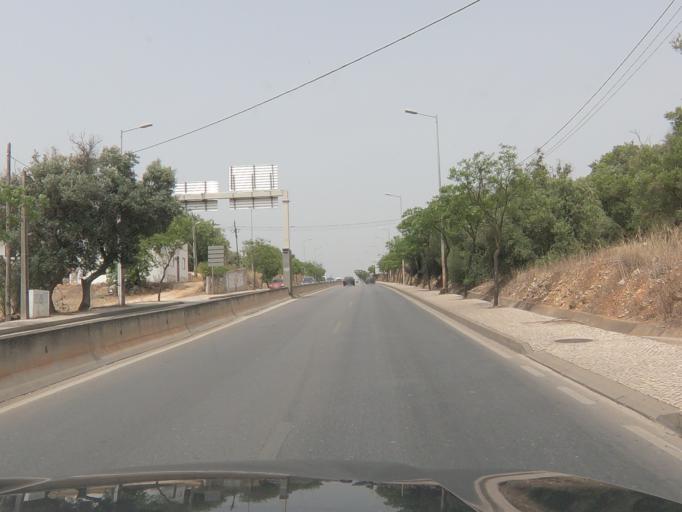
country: PT
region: Faro
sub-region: Portimao
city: Portimao
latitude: 37.1509
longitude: -8.5393
